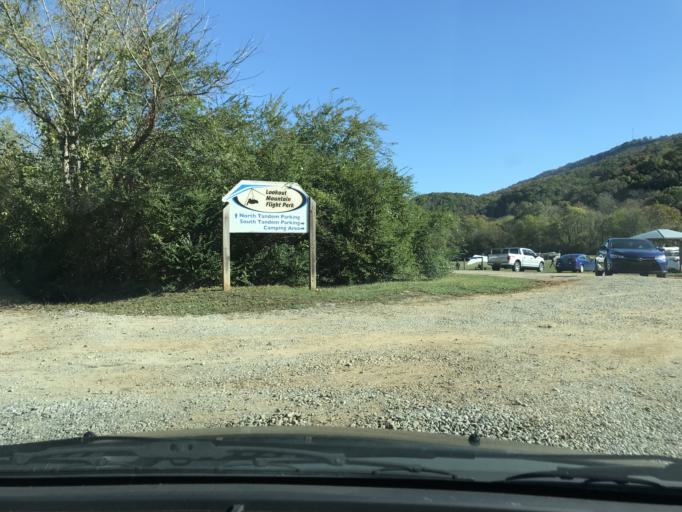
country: US
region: Georgia
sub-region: Dade County
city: Trenton
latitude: 34.8998
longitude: -85.4616
